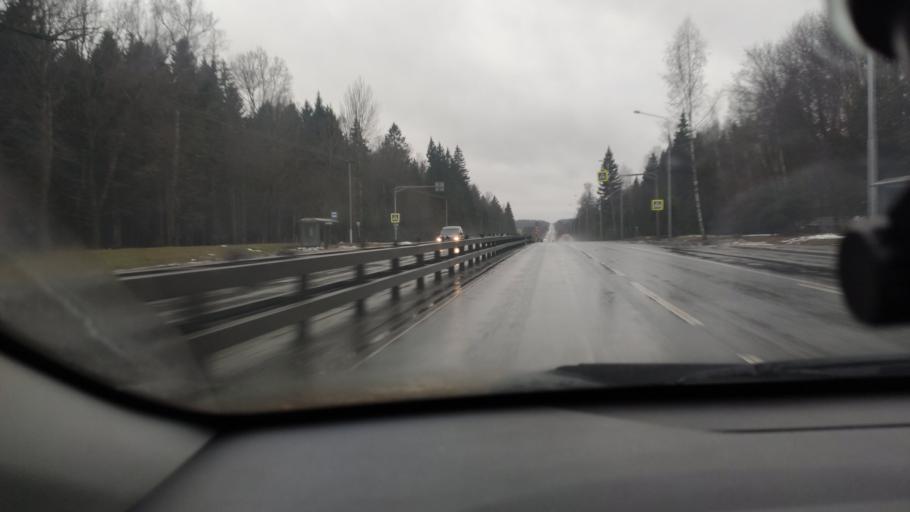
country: RU
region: Moskovskaya
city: Troitsk
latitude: 55.3441
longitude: 37.3179
